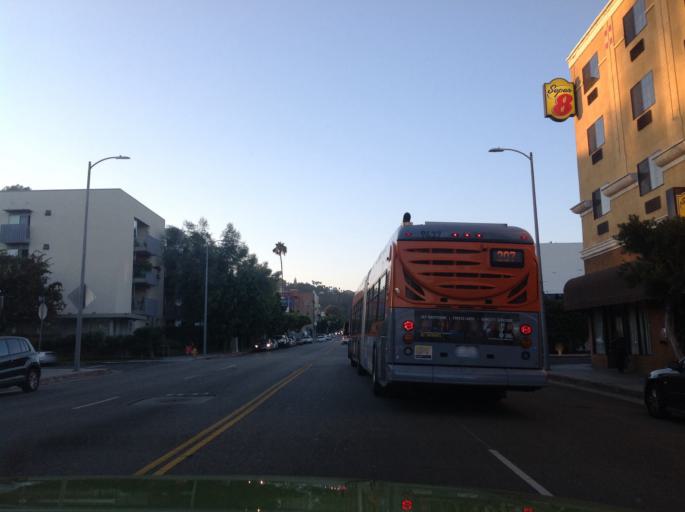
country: US
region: California
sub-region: Los Angeles County
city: Hollywood
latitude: 34.0990
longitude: -118.3092
